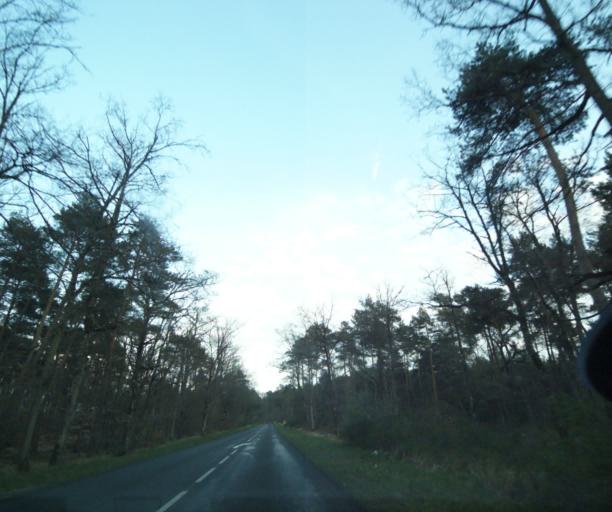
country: FR
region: Ile-de-France
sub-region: Departement de Seine-et-Marne
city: Avon
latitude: 48.3741
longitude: 2.7459
